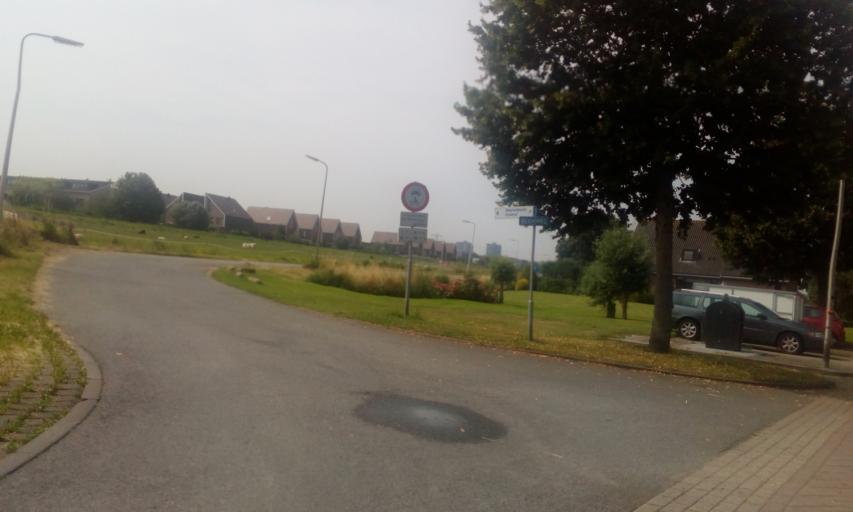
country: NL
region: South Holland
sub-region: Gemeente Krimpen aan den IJssel
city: Krimpen aan den IJssel
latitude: 51.9565
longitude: 4.6121
